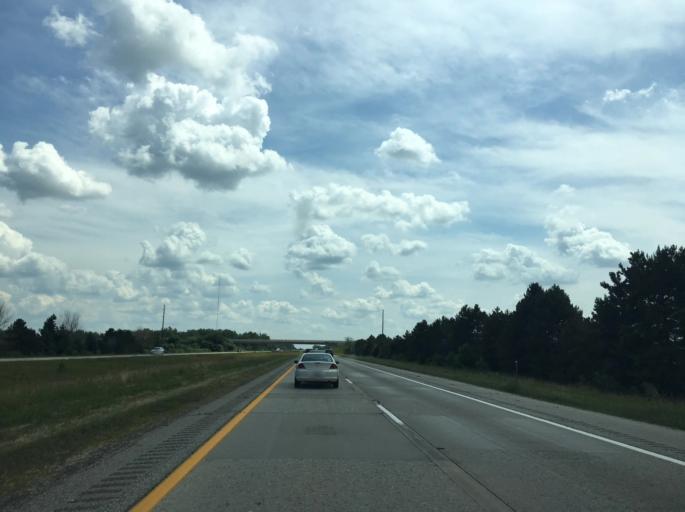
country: US
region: Michigan
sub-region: Bay County
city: Auburn
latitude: 43.7139
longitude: -84.0125
